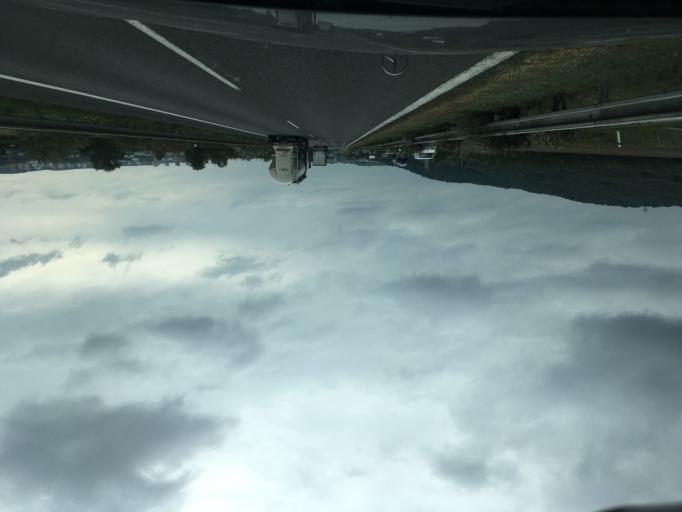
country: SK
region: Bratislavsky
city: Stupava
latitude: 48.2228
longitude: 17.0274
